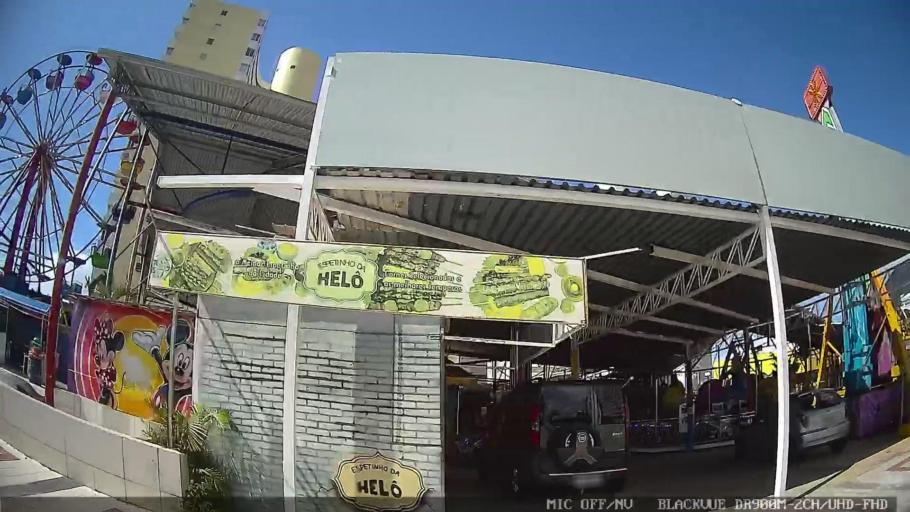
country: BR
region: Sao Paulo
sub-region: Peruibe
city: Peruibe
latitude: -24.3239
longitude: -46.9965
